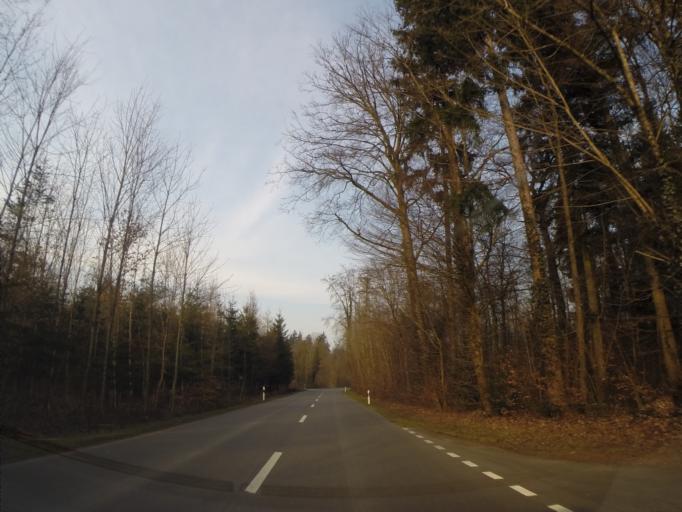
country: CH
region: Zurich
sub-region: Bezirk Andelfingen
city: Kleinandelfingen
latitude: 47.6422
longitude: 8.7092
